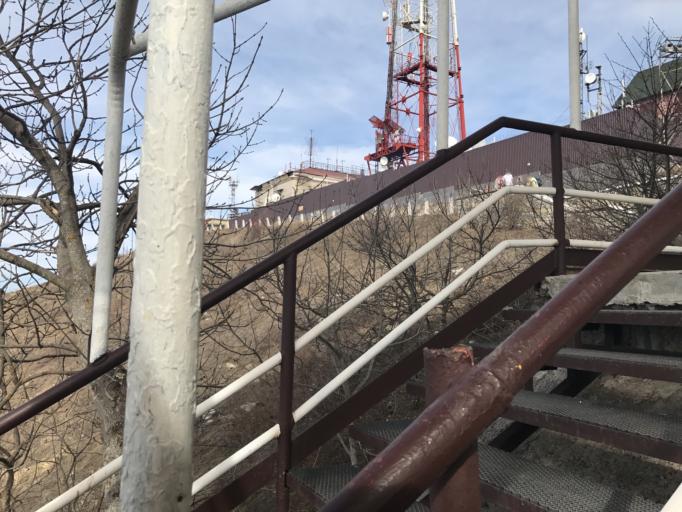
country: RU
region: Stavropol'skiy
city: Goryachevodskiy
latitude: 44.0496
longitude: 43.0887
